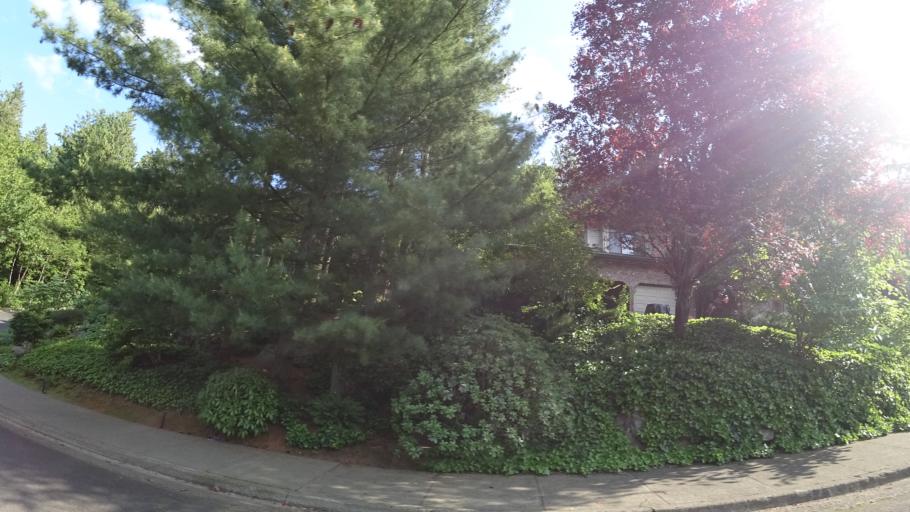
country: US
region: Oregon
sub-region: Washington County
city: Garden Home-Whitford
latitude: 45.4594
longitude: -122.7370
